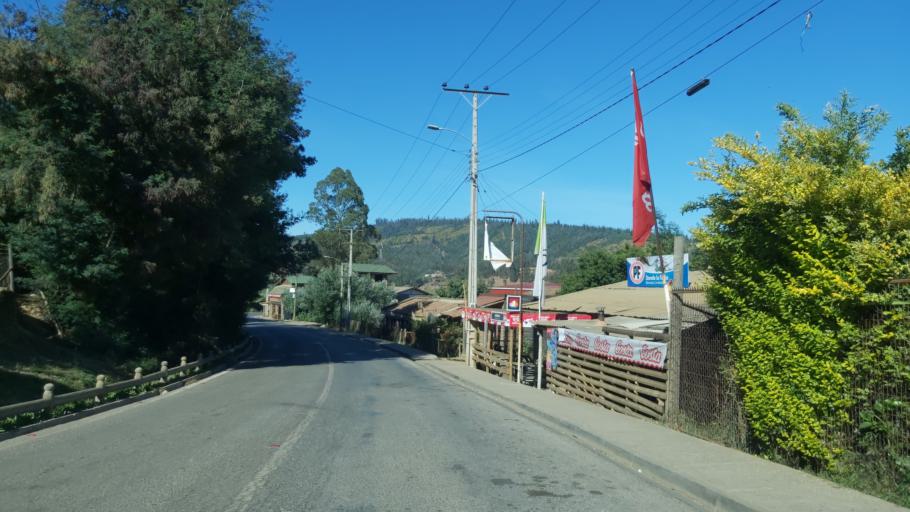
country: CL
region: Maule
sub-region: Provincia de Talca
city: Constitucion
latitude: -34.8511
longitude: -72.0384
